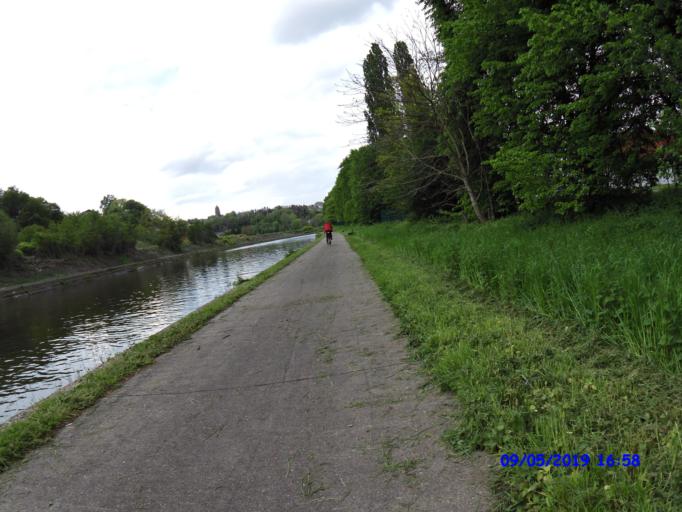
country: BE
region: Wallonia
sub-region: Province de Namur
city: Namur
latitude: 50.4645
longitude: 4.8342
